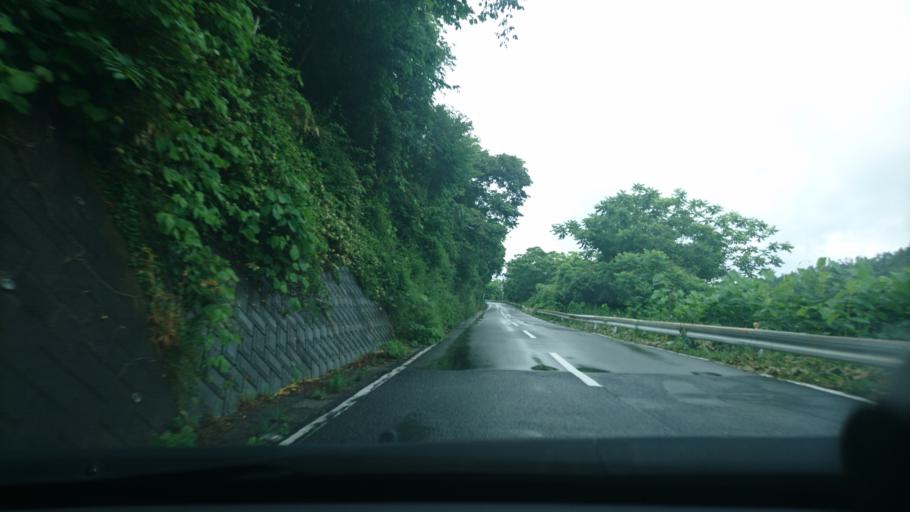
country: JP
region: Miyagi
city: Wakuya
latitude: 38.6767
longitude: 141.2837
